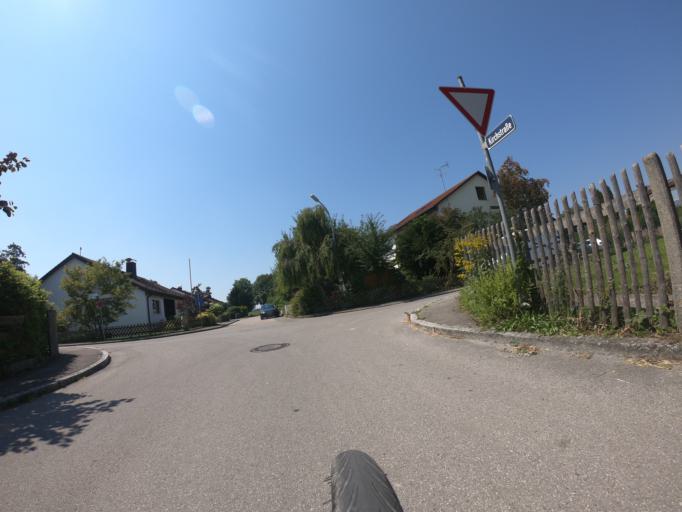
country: DE
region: Bavaria
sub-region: Upper Bavaria
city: Fuerstenfeldbruck
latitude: 48.1508
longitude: 11.2561
